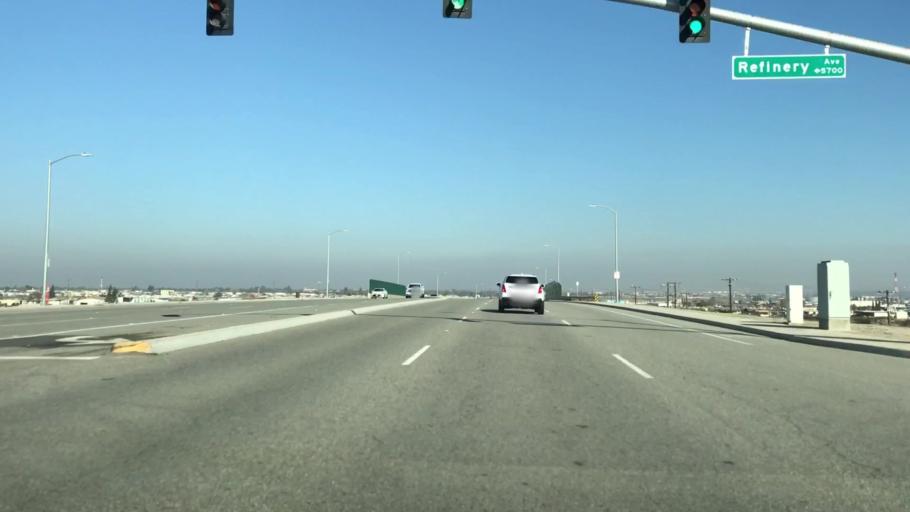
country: US
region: California
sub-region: Kern County
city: Greenacres
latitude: 35.3748
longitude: -119.0659
